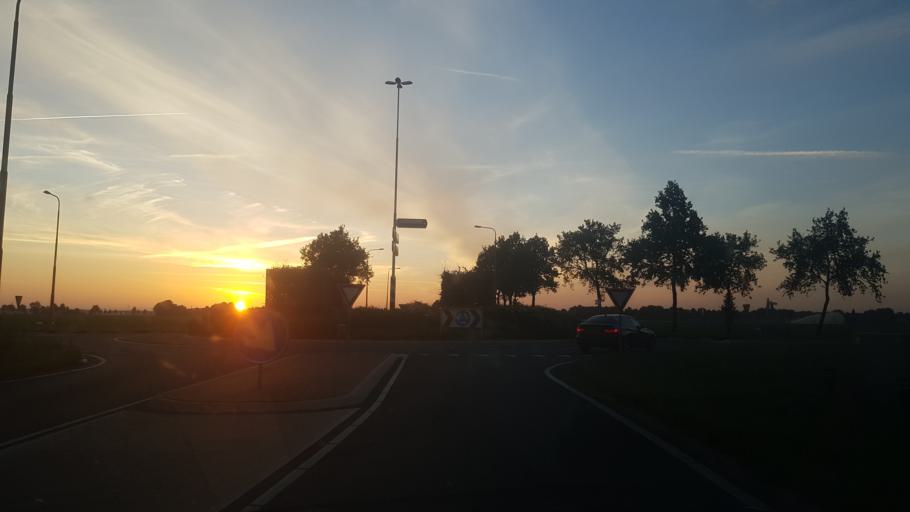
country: NL
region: Flevoland
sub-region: Gemeente Noordoostpolder
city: Emmeloord
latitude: 52.6897
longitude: 5.7347
